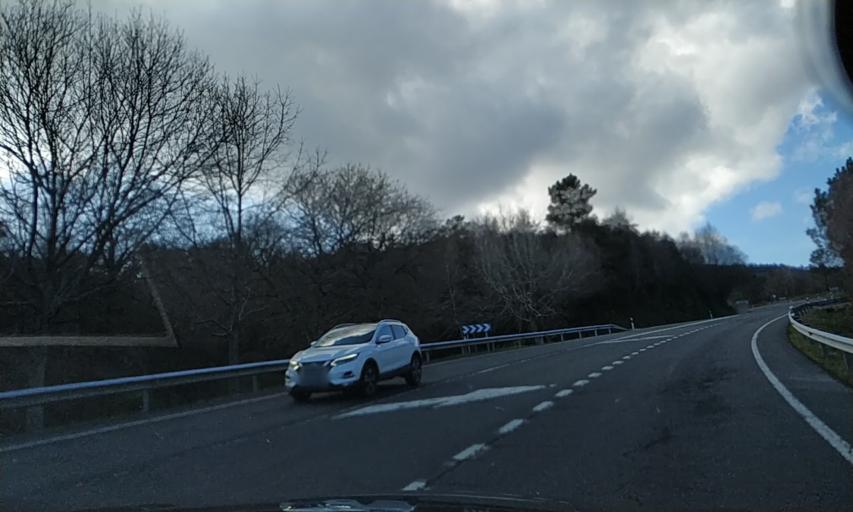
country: ES
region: Galicia
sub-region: Provincia de Pontevedra
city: Silleda
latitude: 42.6978
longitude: -8.3312
